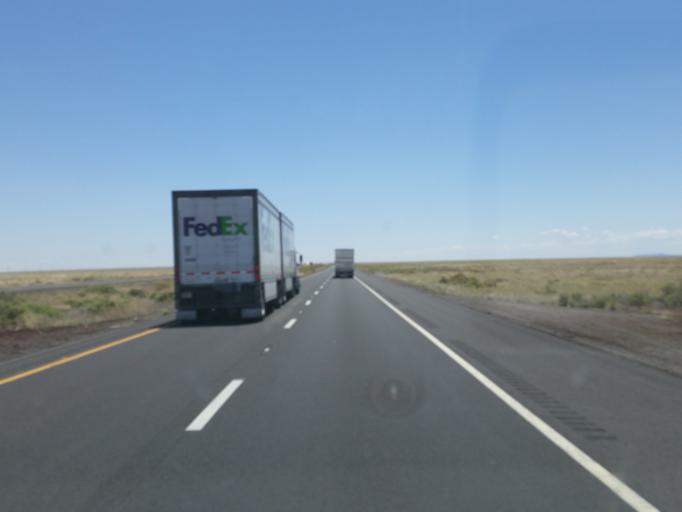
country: US
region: Arizona
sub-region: Coconino County
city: Flagstaff
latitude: 35.1508
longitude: -111.2436
